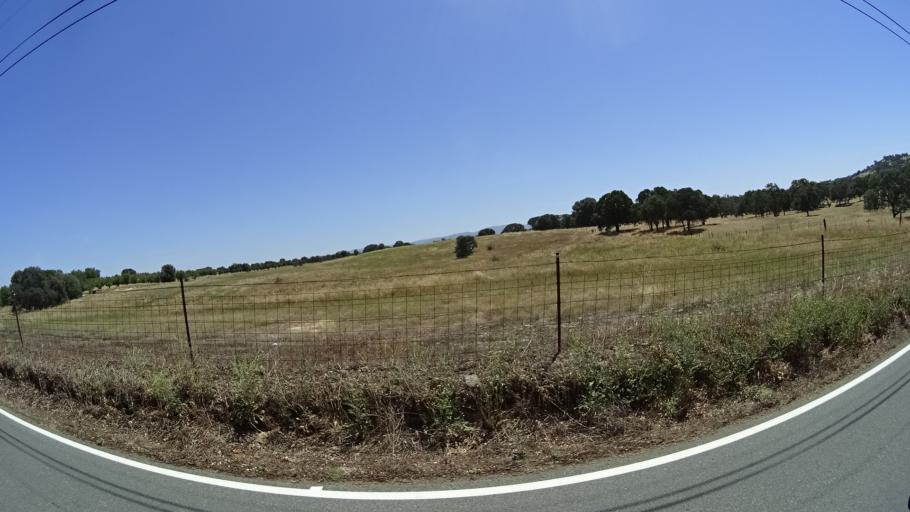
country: US
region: California
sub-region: Calaveras County
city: Rancho Calaveras
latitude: 38.1391
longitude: -120.9134
